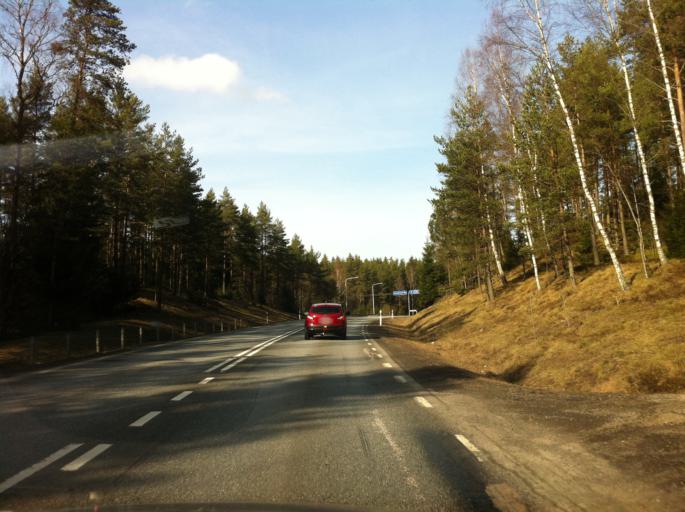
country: SE
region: Joenkoeping
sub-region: Mullsjo Kommun
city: Mullsjoe
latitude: 57.9824
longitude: 13.8305
